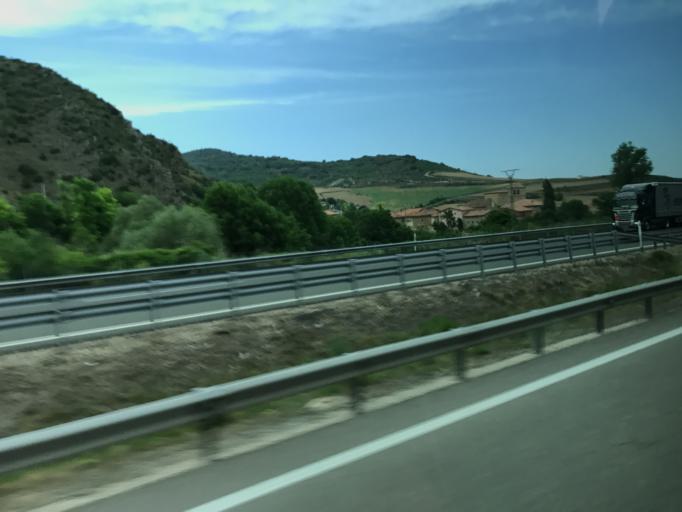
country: ES
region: Castille and Leon
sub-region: Provincia de Burgos
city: Ameyugo
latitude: 42.6531
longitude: -3.0627
